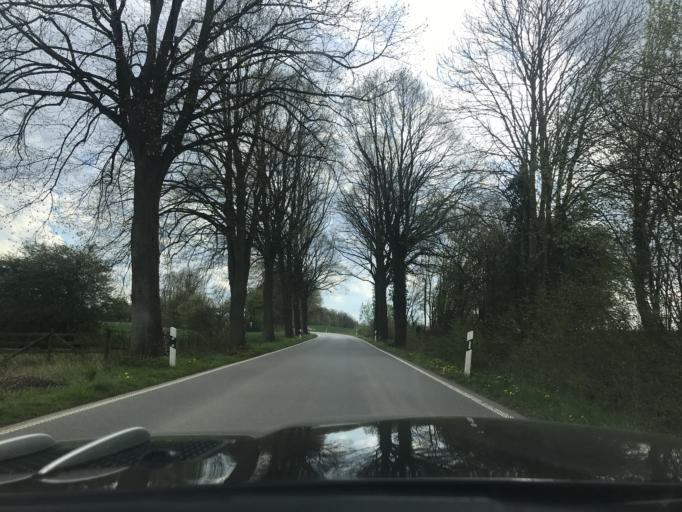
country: DE
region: Schleswig-Holstein
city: Timmendorfer Strand
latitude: 53.9469
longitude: 10.7896
